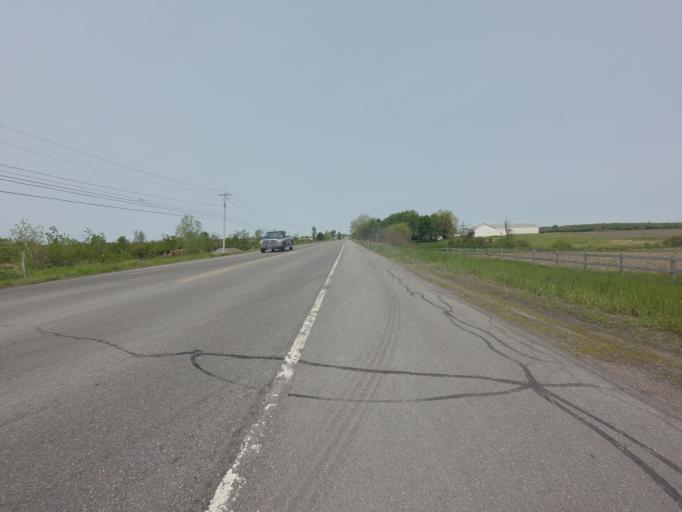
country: US
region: New York
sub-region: Jefferson County
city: Dexter
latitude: 44.0500
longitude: -76.0979
